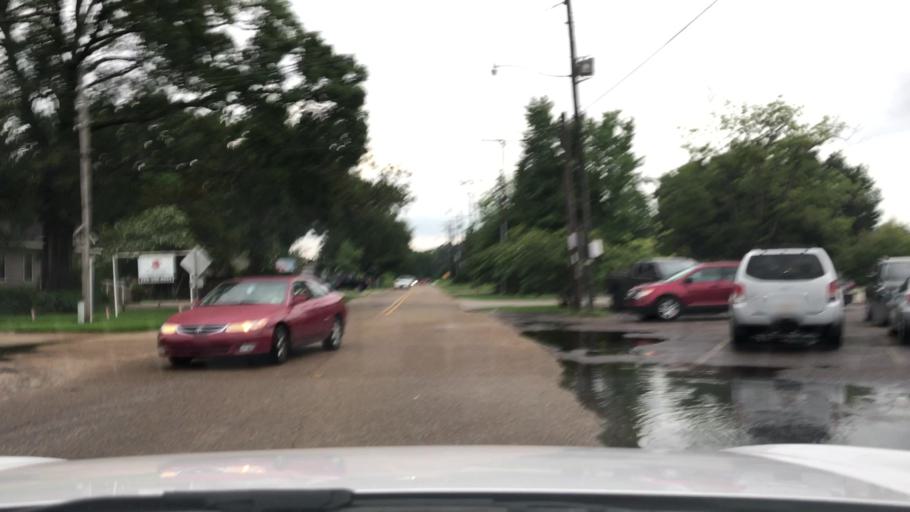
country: US
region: Louisiana
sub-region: East Baton Rouge Parish
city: Merrydale
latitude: 30.4803
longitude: -91.1176
